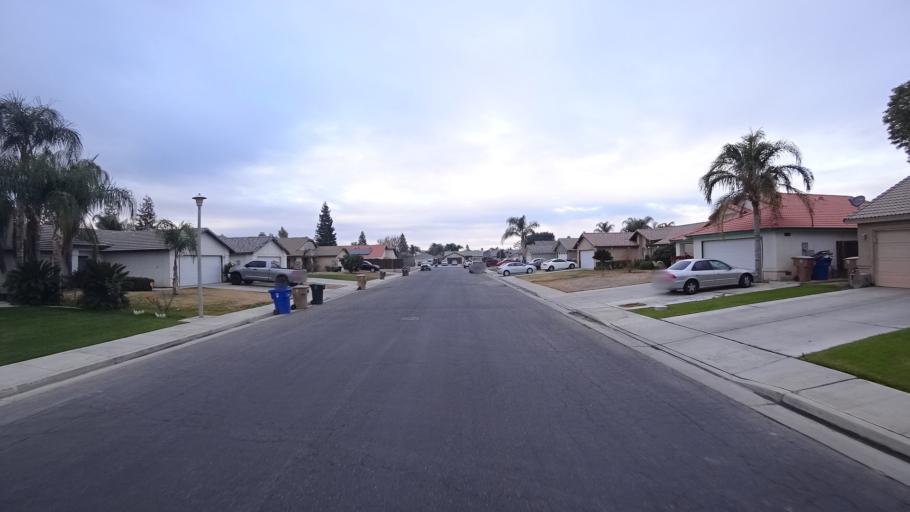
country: US
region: California
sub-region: Kern County
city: Greenfield
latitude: 35.3020
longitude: -119.0759
